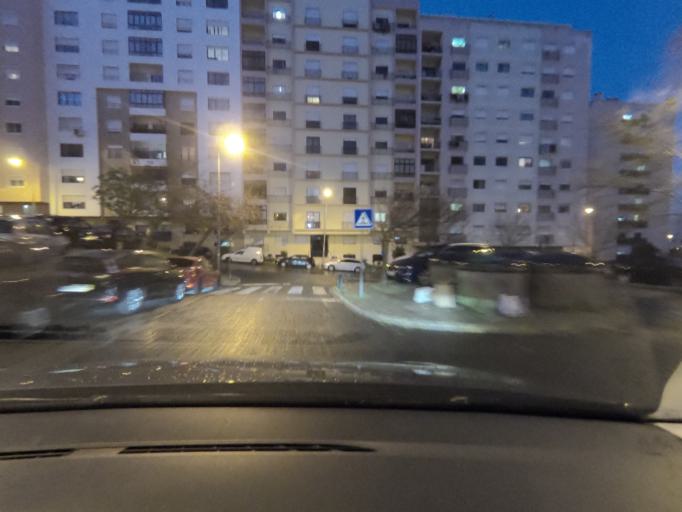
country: PT
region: Lisbon
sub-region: Sintra
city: Cacem
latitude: 38.7488
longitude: -9.2981
